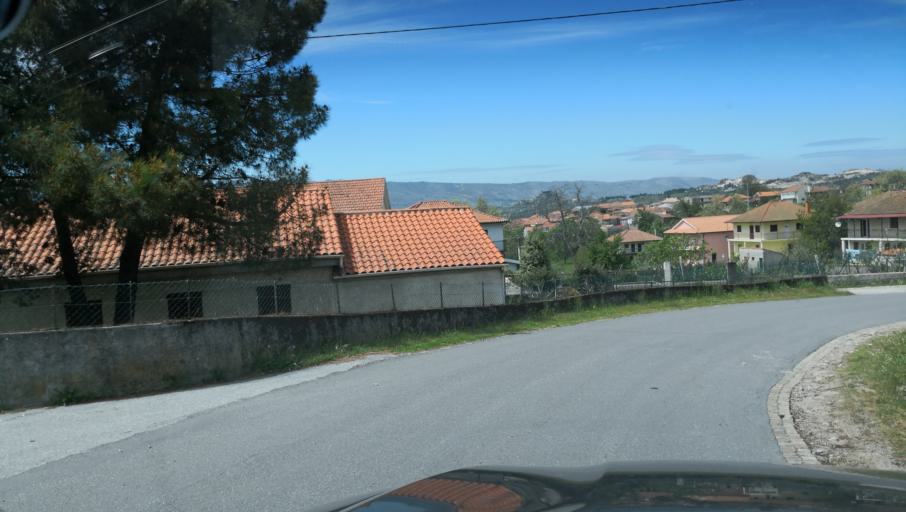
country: PT
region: Vila Real
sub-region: Vila Real
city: Vila Real
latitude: 41.3564
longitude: -7.6649
